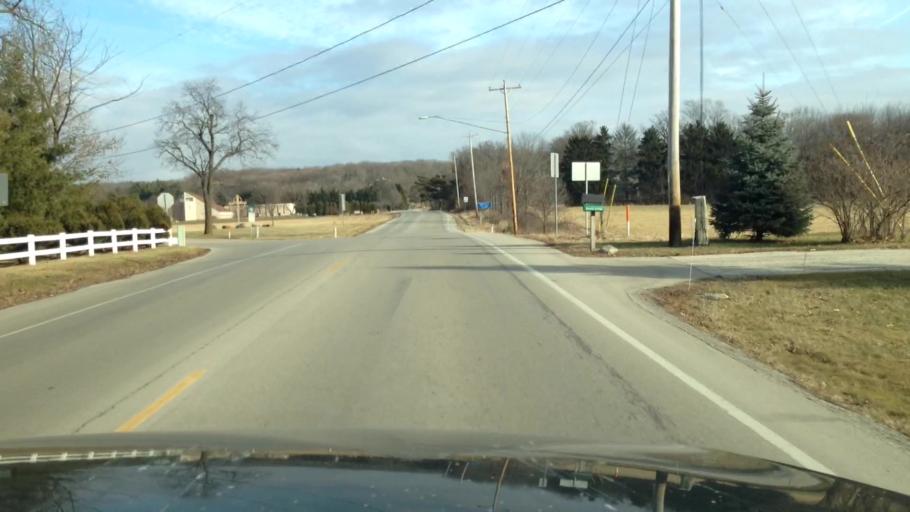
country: US
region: Wisconsin
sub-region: Waukesha County
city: Muskego
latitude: 42.9300
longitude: -88.1394
